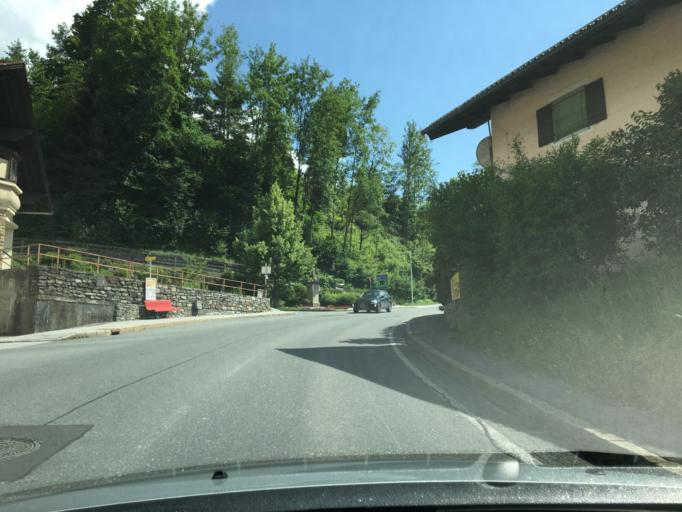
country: AT
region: Salzburg
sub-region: Politischer Bezirk Sankt Johann im Pongau
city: Sankt Johann im Pongau
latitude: 47.3532
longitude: 13.2068
